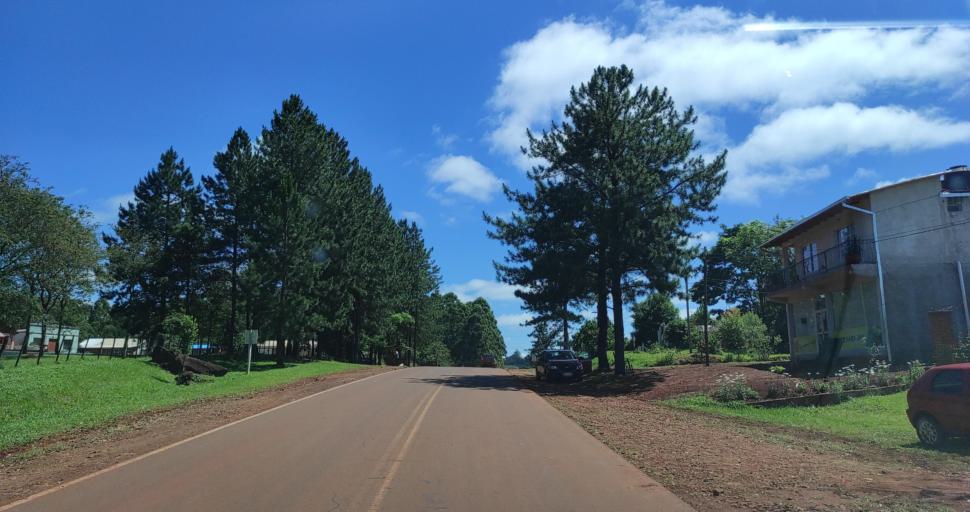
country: AR
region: Misiones
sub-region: Departamento de Veinticinco de Mayo
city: Veinticinco de Mayo
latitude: -27.3941
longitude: -54.7496
